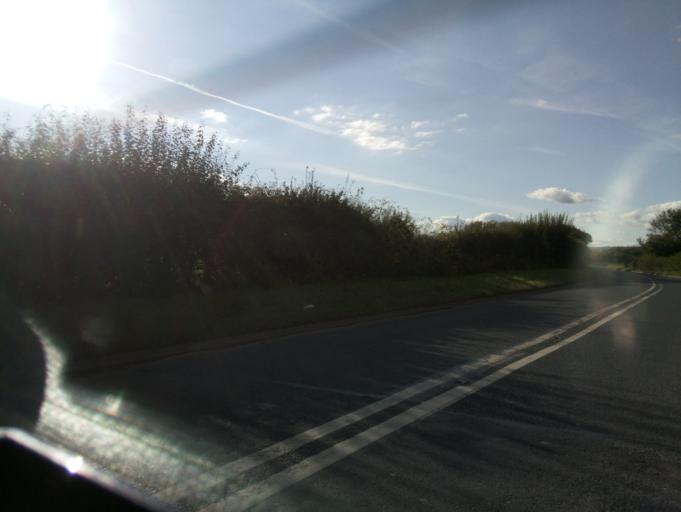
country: GB
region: England
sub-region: Herefordshire
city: Kinnersley
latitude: 52.1210
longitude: -2.9961
